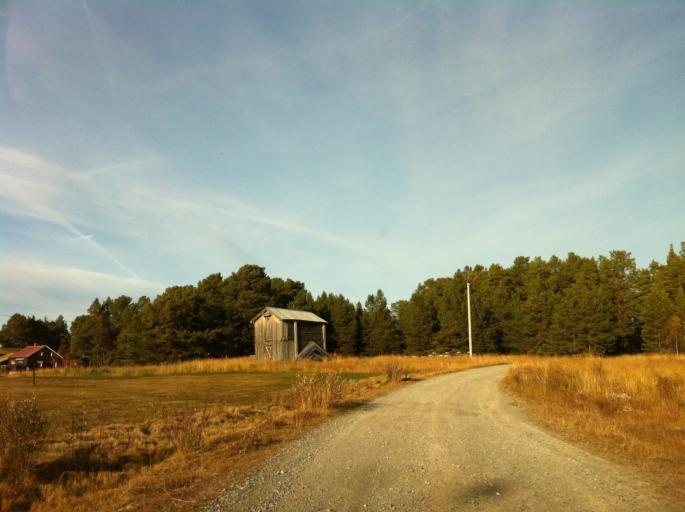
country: NO
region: Hedmark
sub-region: Engerdal
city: Engerdal
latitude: 62.1691
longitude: 11.9424
